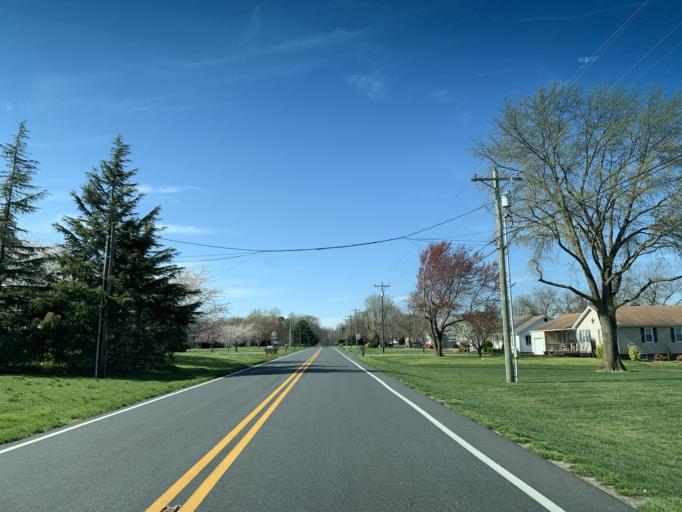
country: US
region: Delaware
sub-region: Sussex County
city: Milford
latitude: 38.9393
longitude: -75.4597
